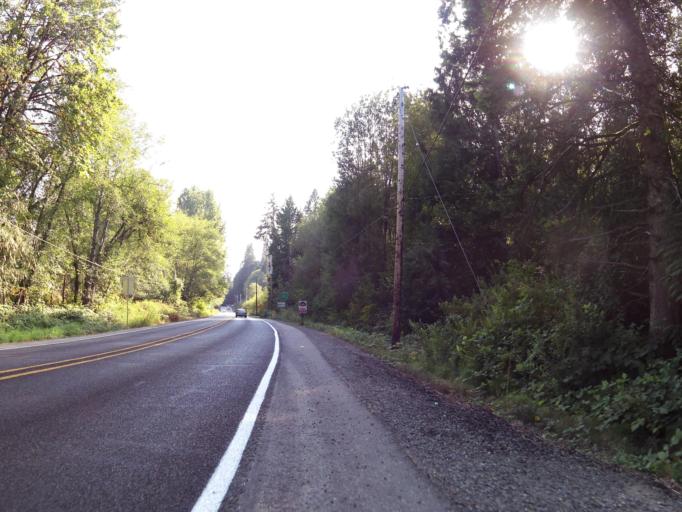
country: US
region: Washington
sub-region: Mason County
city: Belfair
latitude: 47.5013
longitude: -122.8010
